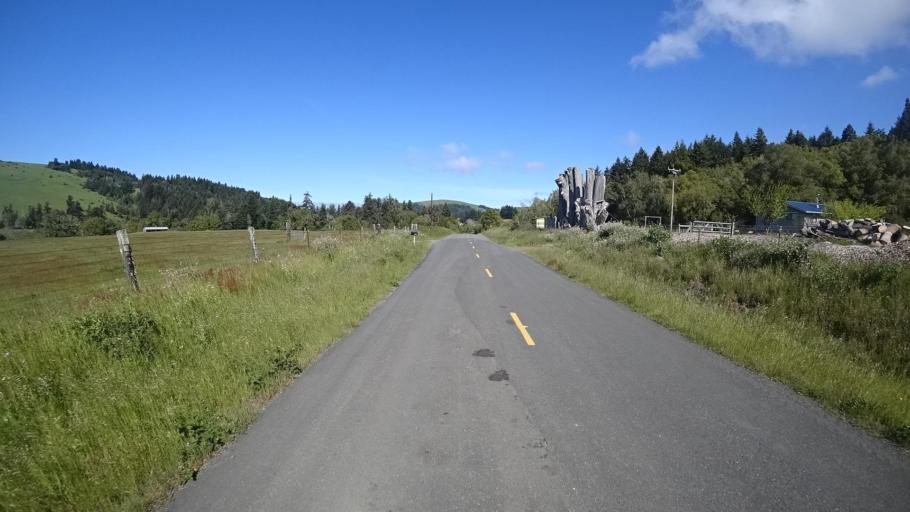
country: US
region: California
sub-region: Humboldt County
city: Ferndale
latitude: 40.3400
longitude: -124.3151
